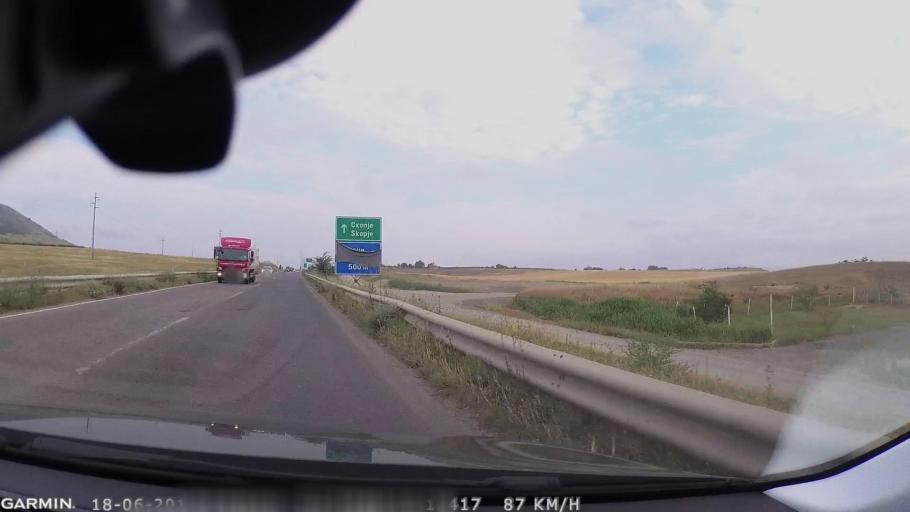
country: MK
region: Stip
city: Shtip
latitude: 41.7770
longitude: 22.1333
